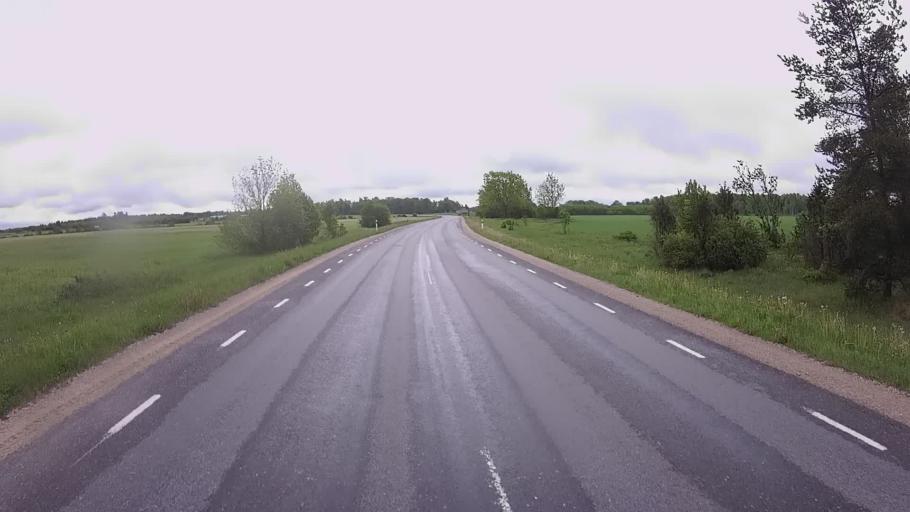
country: EE
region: Harju
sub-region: Nissi vald
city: Turba
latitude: 58.8996
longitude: 24.2264
